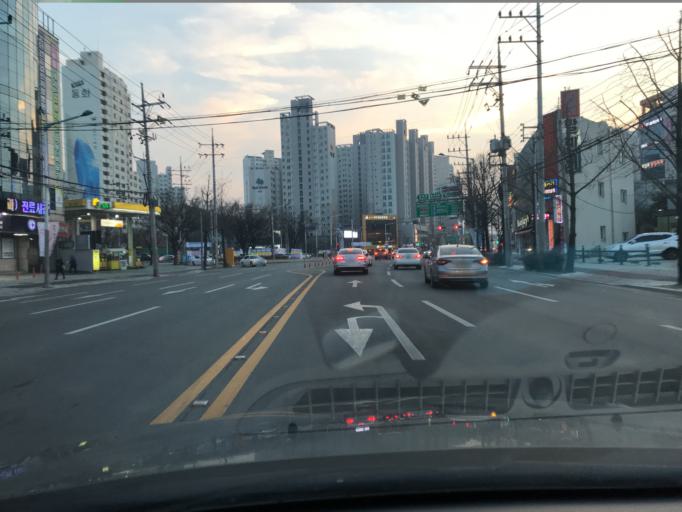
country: KR
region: Daegu
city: Hwawon
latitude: 35.8117
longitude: 128.5172
